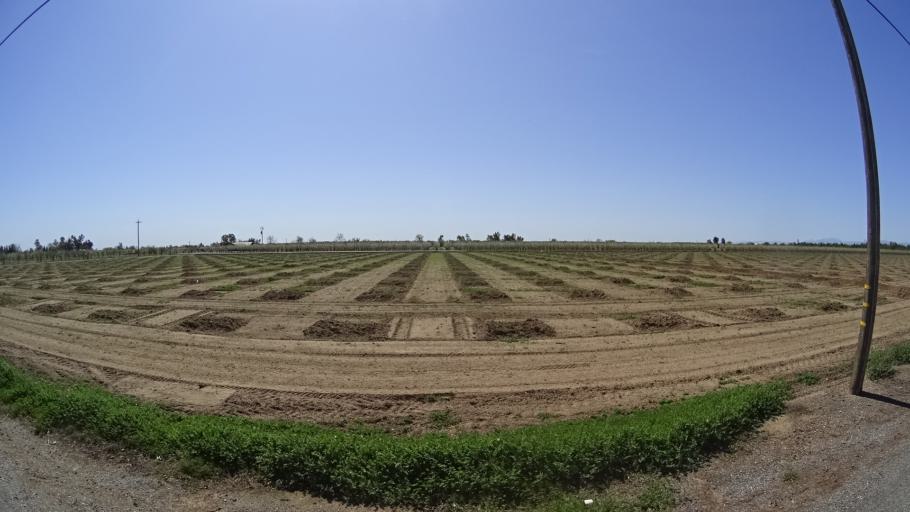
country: US
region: California
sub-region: Glenn County
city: Hamilton City
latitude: 39.7969
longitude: -122.0770
